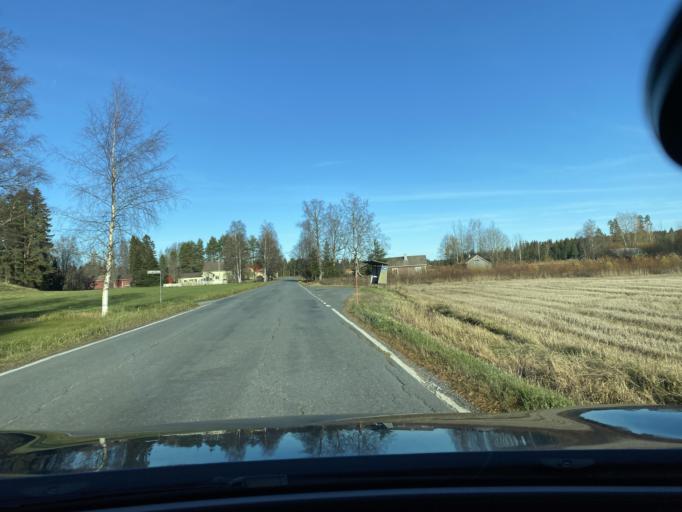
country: FI
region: Haeme
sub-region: Forssa
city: Tammela
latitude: 60.8719
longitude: 23.8462
